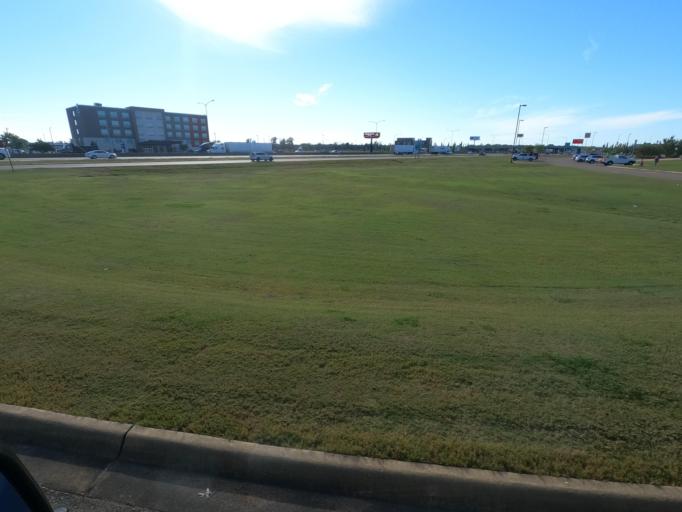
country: US
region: Arkansas
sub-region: Crittenden County
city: West Memphis
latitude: 35.1642
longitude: -90.1716
